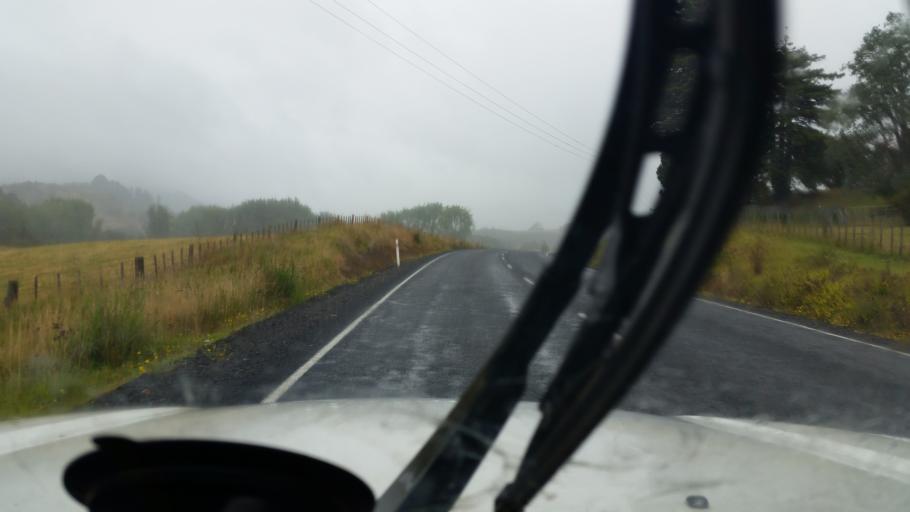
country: NZ
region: Northland
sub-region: Far North District
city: Kaitaia
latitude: -35.2753
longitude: 173.3492
